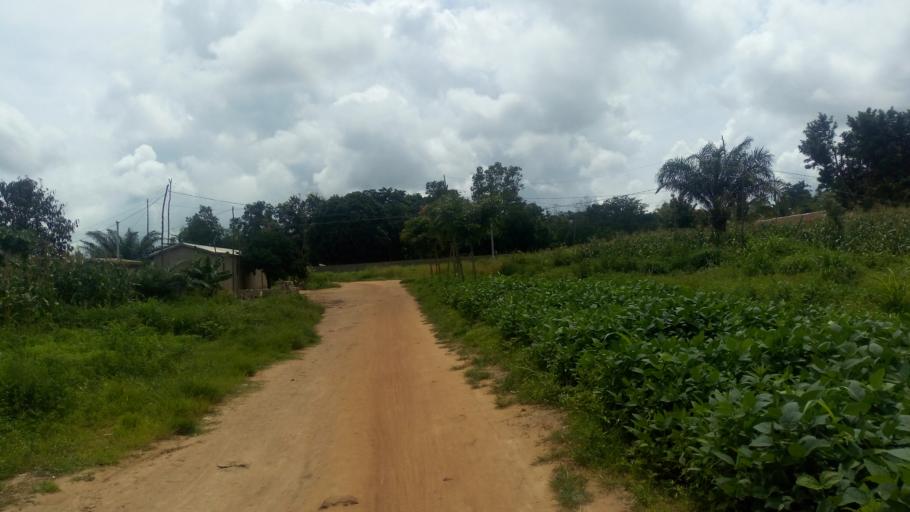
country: TG
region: Centrale
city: Sotouboua
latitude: 8.5561
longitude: 0.9951
